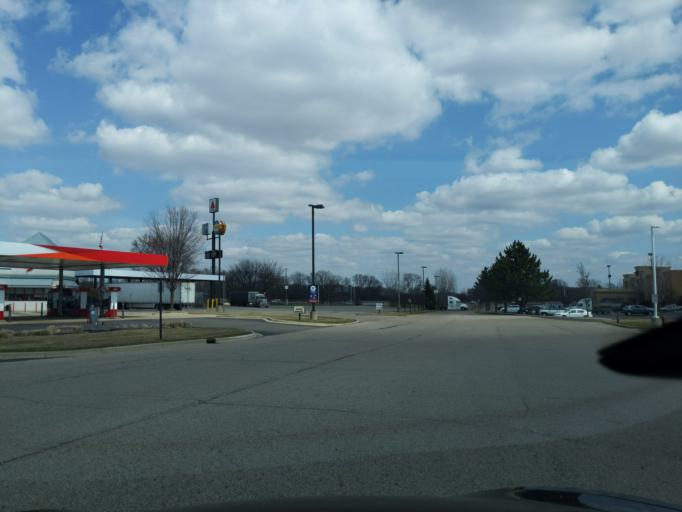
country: US
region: Michigan
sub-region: Calhoun County
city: Marshall
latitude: 42.2916
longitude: -84.9641
